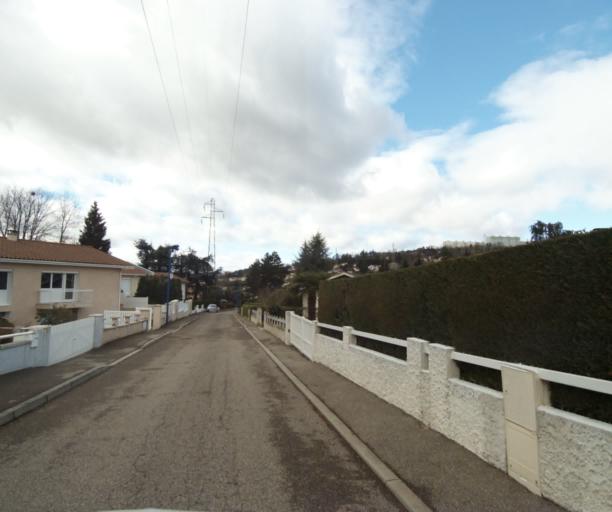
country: FR
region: Rhone-Alpes
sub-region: Departement de la Loire
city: La Talaudiere
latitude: 45.4712
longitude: 4.4147
